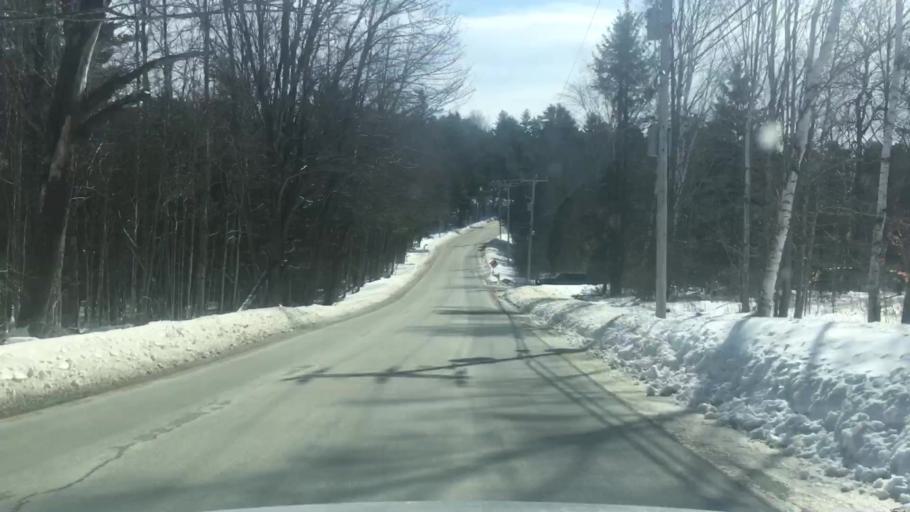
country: US
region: Maine
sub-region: Penobscot County
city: Holden
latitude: 44.7519
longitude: -68.6334
